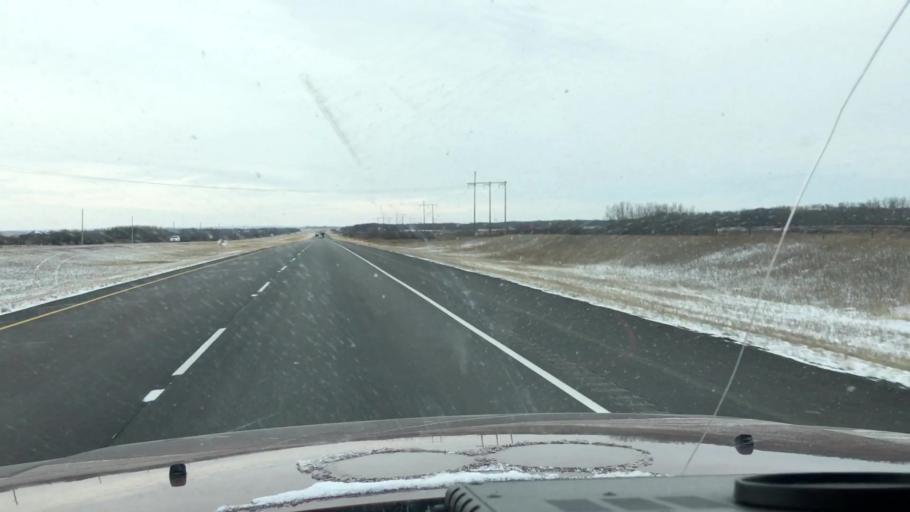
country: CA
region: Saskatchewan
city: Saskatoon
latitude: 51.8929
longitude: -106.5181
